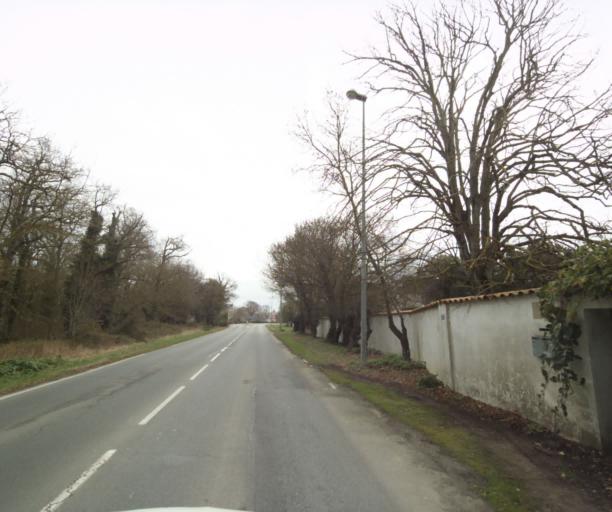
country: FR
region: Poitou-Charentes
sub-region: Departement de la Charente-Maritime
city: Lagord
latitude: 46.1854
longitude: -1.1769
